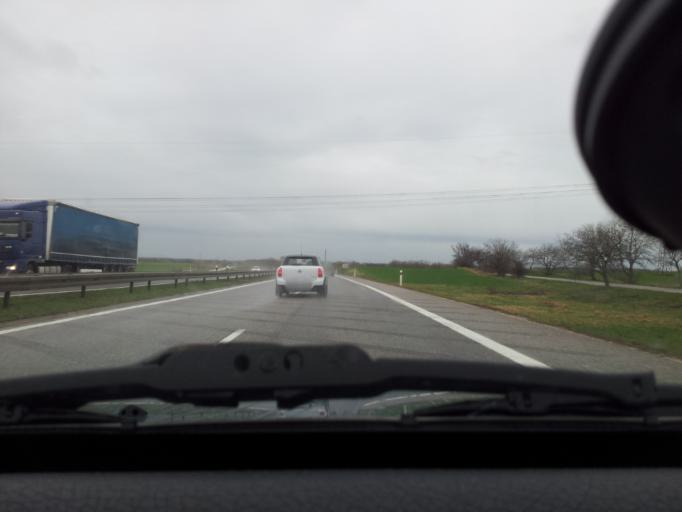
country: SK
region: Nitriansky
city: Sellye
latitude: 48.2805
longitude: 17.8469
